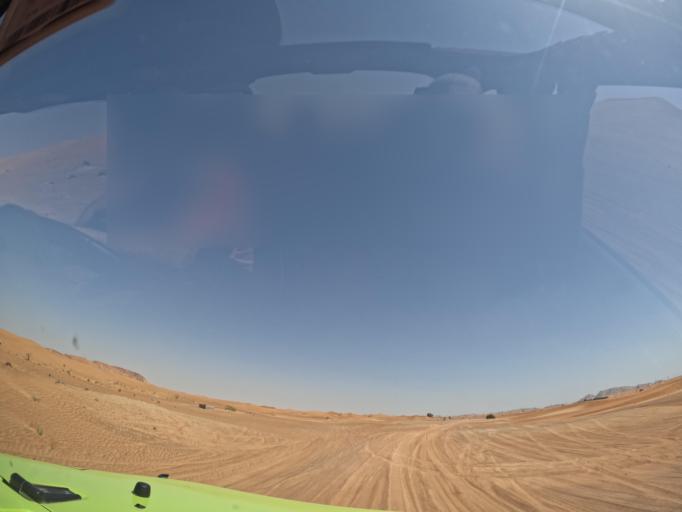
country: AE
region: Ash Shariqah
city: Adh Dhayd
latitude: 25.0030
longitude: 55.7322
